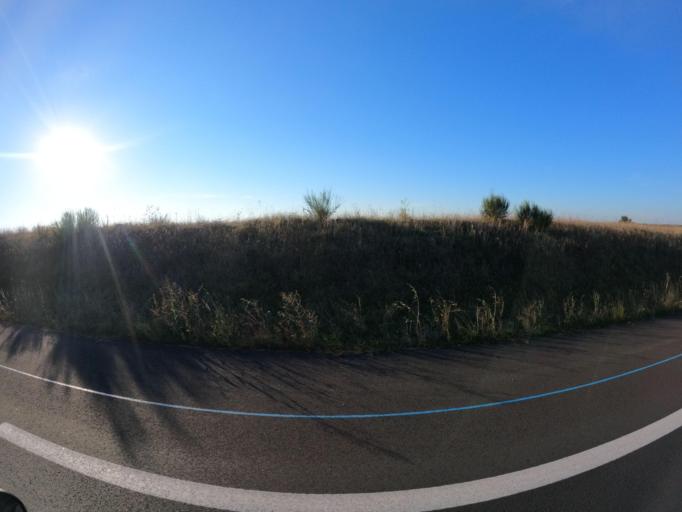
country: FR
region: Pays de la Loire
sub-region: Departement de la Vendee
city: Mortagne-sur-Sevre
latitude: 46.9930
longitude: -0.9137
